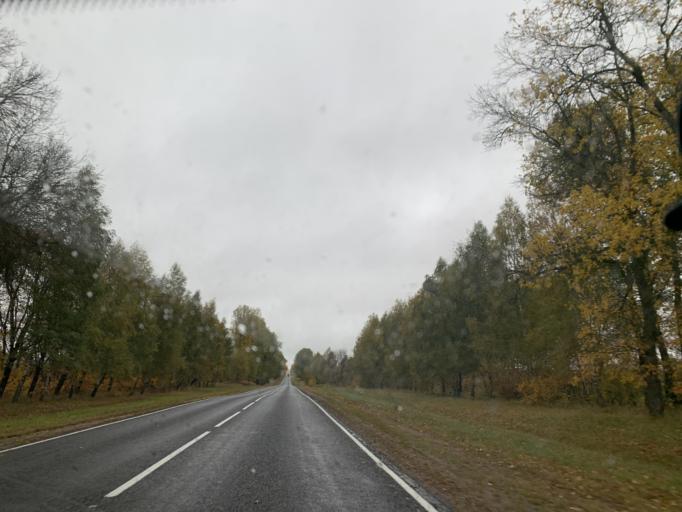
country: BY
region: Minsk
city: Novy Svyerzhan'
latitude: 53.4270
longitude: 26.6368
